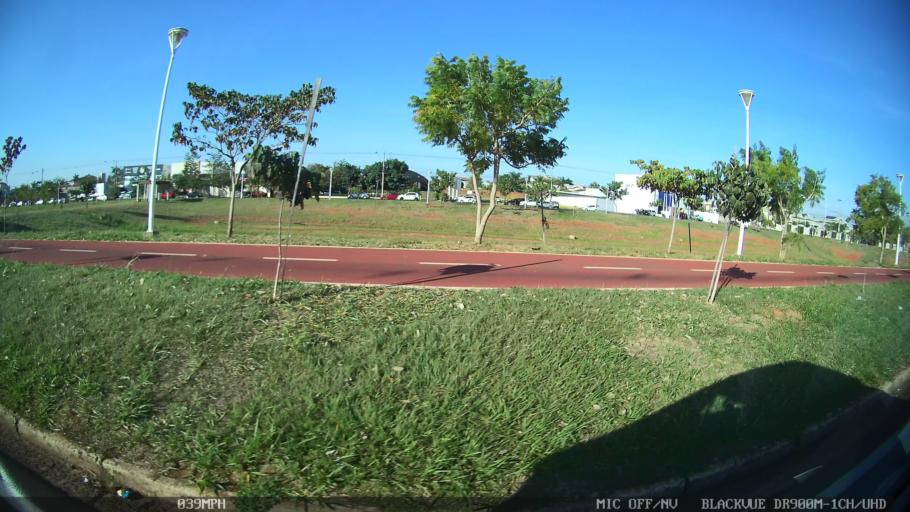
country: BR
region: Sao Paulo
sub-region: Sao Jose Do Rio Preto
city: Sao Jose do Rio Preto
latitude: -20.8579
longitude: -49.4124
